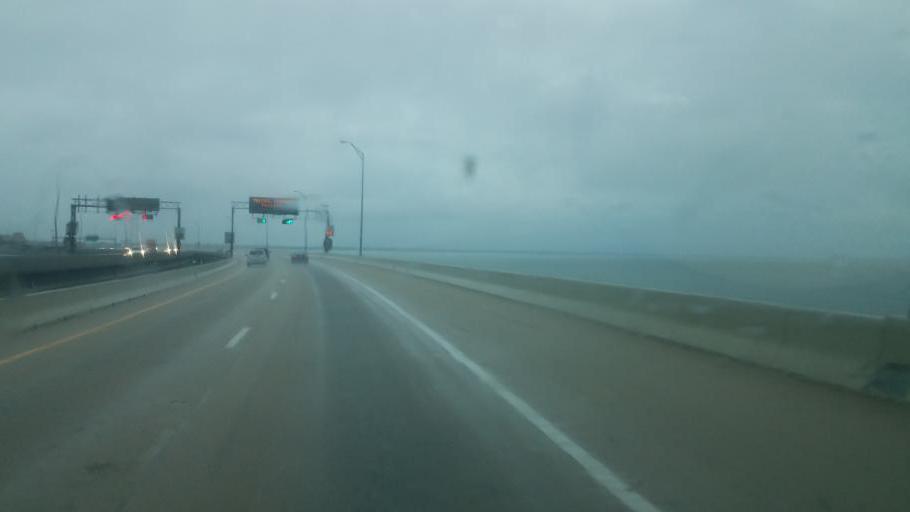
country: US
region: Virginia
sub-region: City of Newport News
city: Newport News
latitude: 36.9394
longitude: -76.4024
